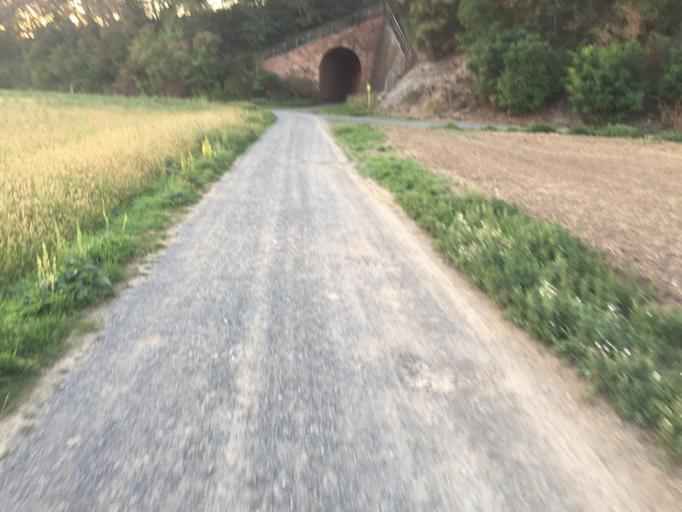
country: DE
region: Hesse
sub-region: Regierungsbezirk Giessen
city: Heuchelheim
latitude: 50.5638
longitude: 8.6404
